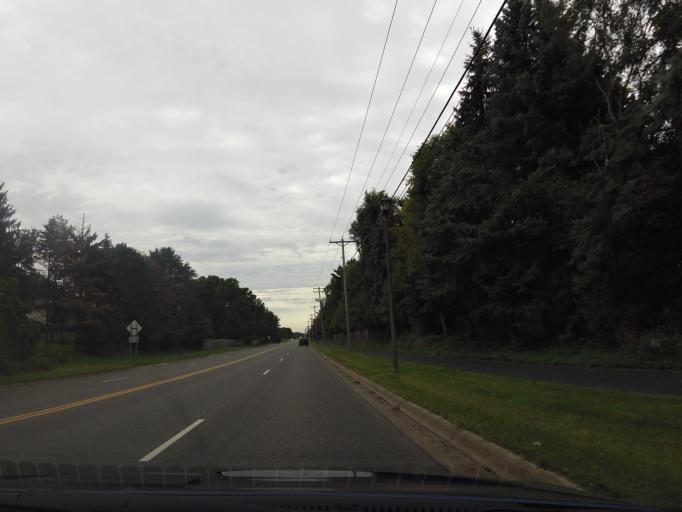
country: US
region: Minnesota
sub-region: Washington County
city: Cottage Grove
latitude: 44.8448
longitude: -92.9493
